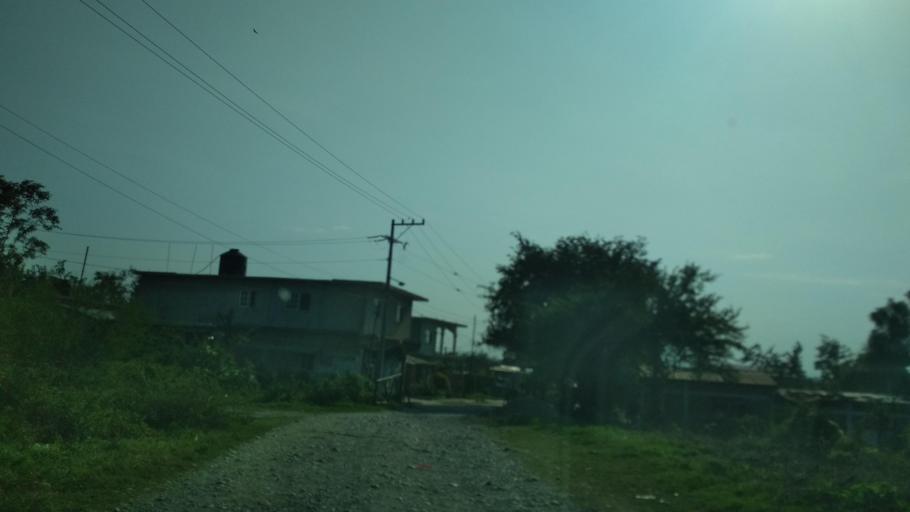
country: MM
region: Shan
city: Taunggyi
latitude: 20.4000
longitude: 97.3324
